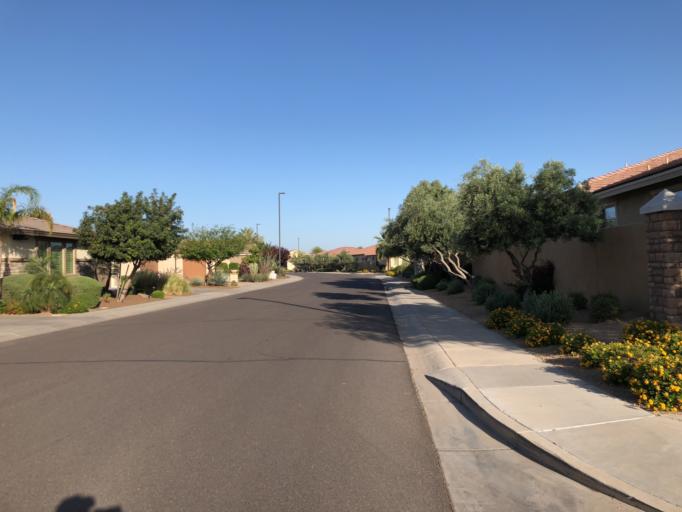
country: US
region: Arizona
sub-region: Maricopa County
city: Queen Creek
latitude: 33.2299
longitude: -111.7127
